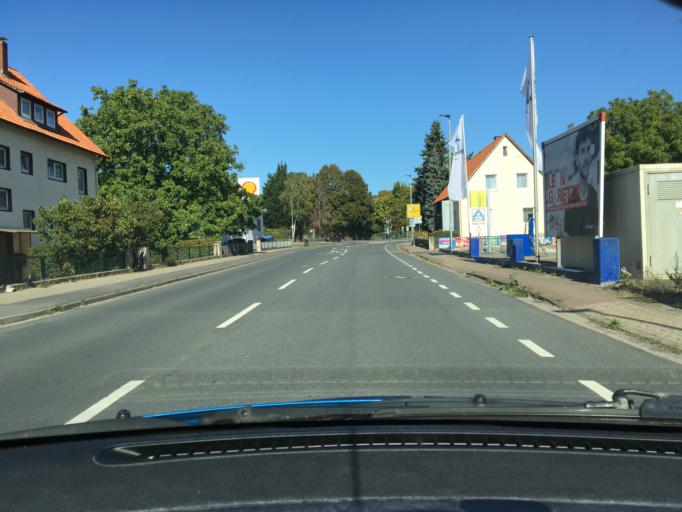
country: DE
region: Lower Saxony
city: Springe
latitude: 52.2095
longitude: 9.5678
